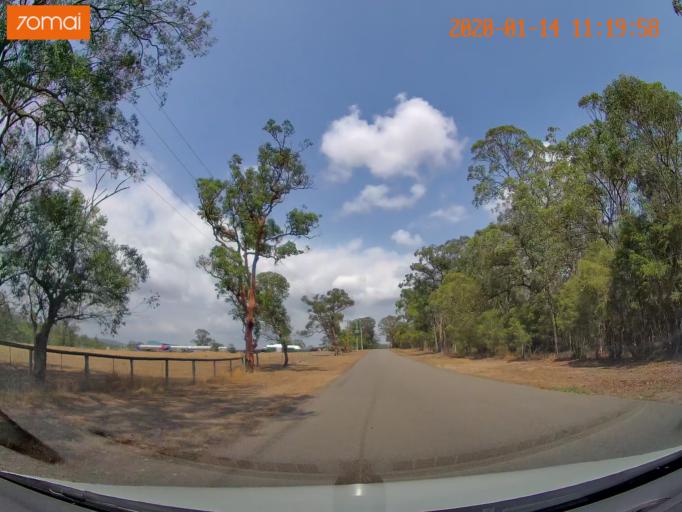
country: AU
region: New South Wales
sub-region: Lake Macquarie Shire
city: Cooranbong
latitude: -33.1003
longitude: 151.4587
